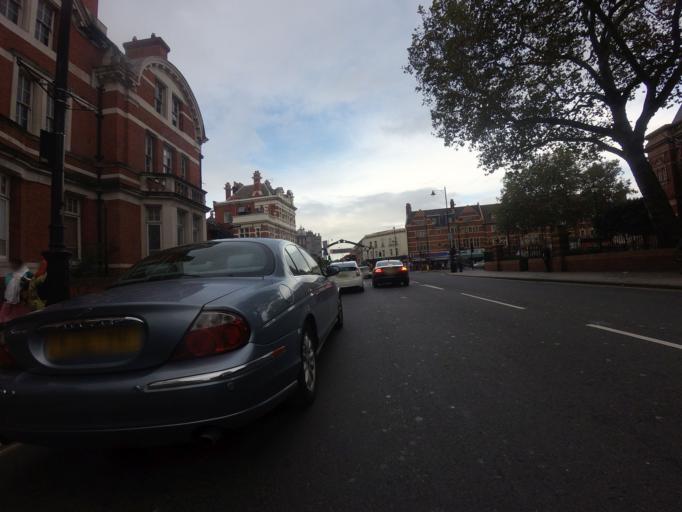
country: GB
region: England
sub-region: Greater London
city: East Ham
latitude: 51.5325
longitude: 0.0548
